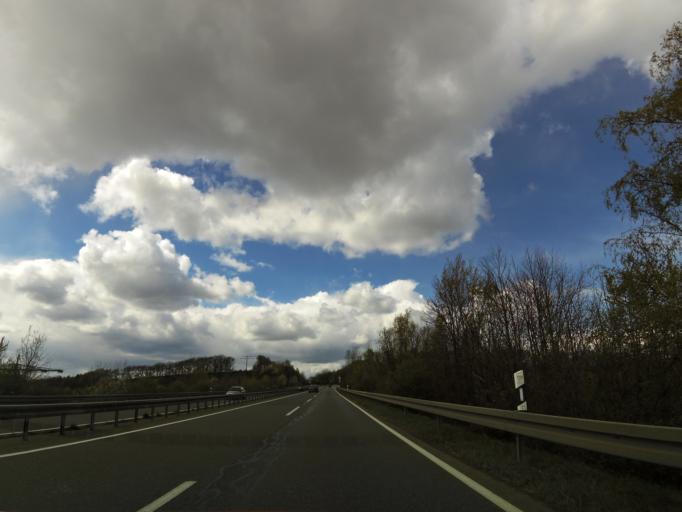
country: DE
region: Lower Saxony
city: Vienenburg
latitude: 51.9291
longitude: 10.4979
